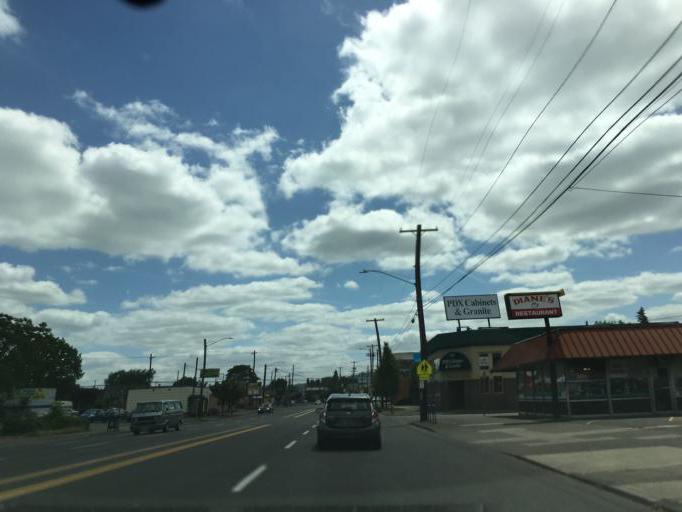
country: US
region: Oregon
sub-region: Multnomah County
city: Lents
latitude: 45.4967
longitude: -122.6106
